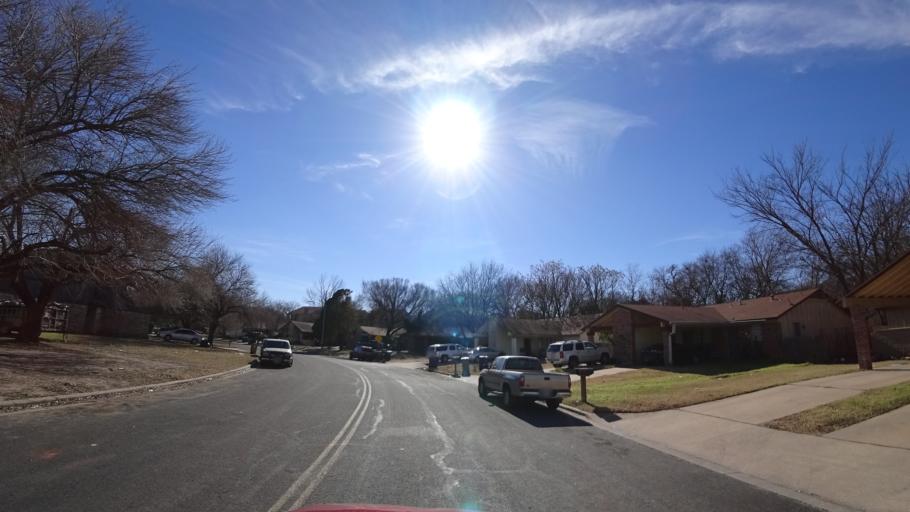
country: US
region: Texas
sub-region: Travis County
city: Wells Branch
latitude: 30.3820
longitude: -97.7112
